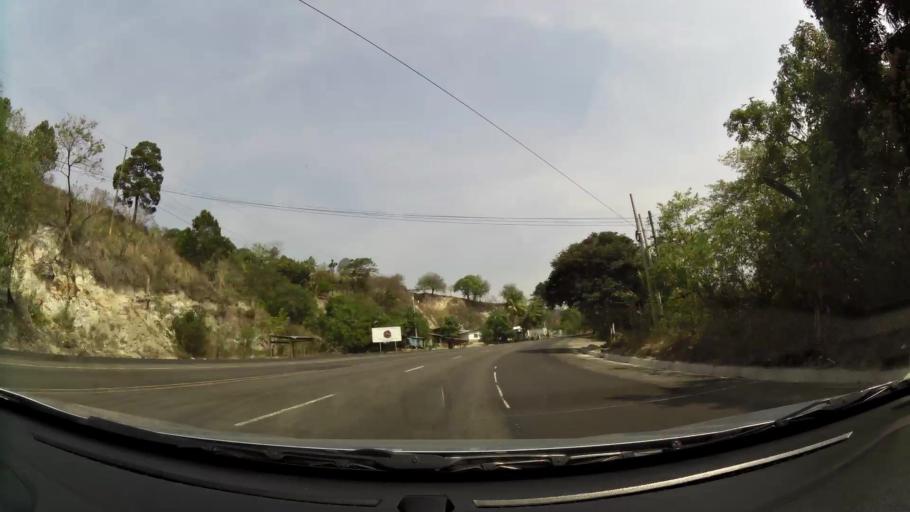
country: HN
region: Comayagua
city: Potrerillos
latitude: 14.5377
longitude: -87.8168
